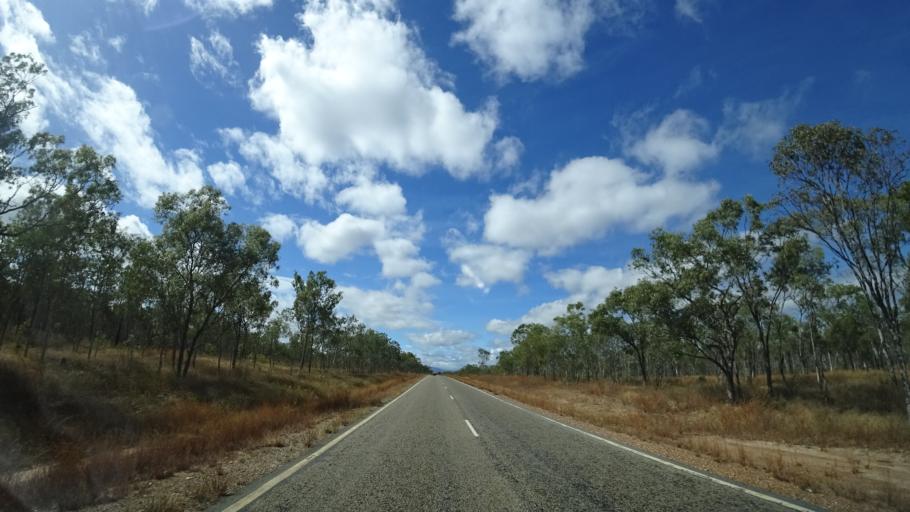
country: AU
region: Queensland
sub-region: Cairns
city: Port Douglas
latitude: -16.4913
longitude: 144.9356
